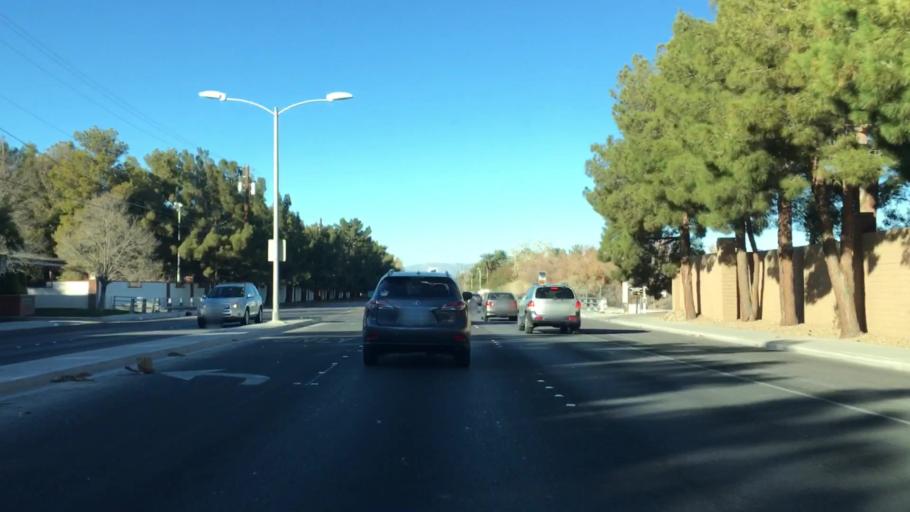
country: US
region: Nevada
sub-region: Clark County
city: Whitney
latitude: 36.0603
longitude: -115.1004
